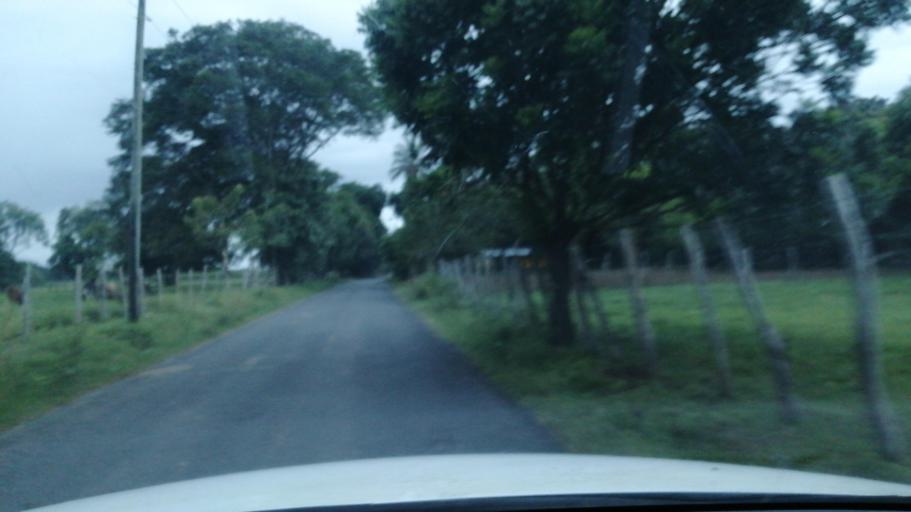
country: PA
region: Chiriqui
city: Alanje
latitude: 8.4023
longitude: -82.4991
